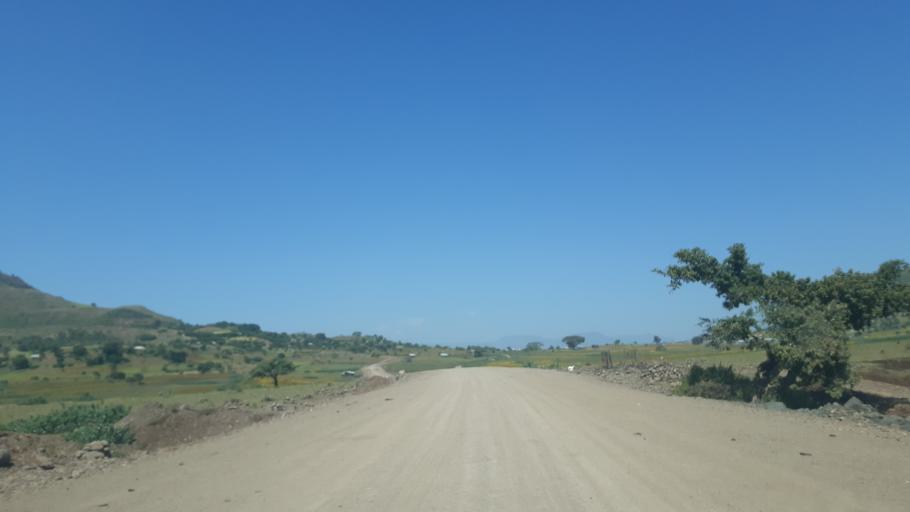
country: ET
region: Amhara
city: Dabat
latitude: 13.1558
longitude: 37.6135
